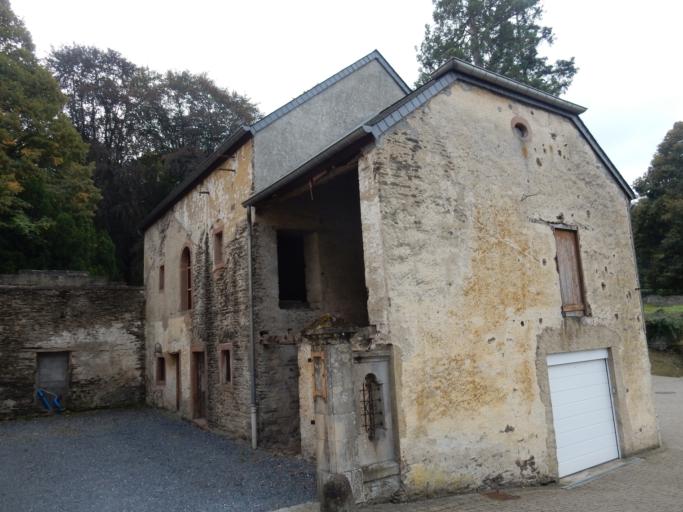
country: LU
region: Diekirch
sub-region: Canton de Wiltz
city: Wiltz
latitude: 49.9671
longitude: 5.9310
